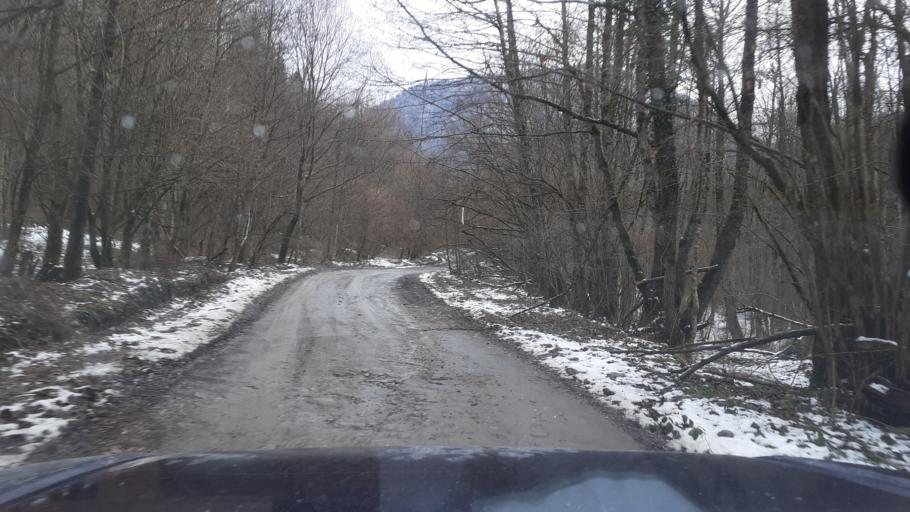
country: RU
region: Krasnodarskiy
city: Neftegorsk
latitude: 44.0670
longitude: 39.7232
